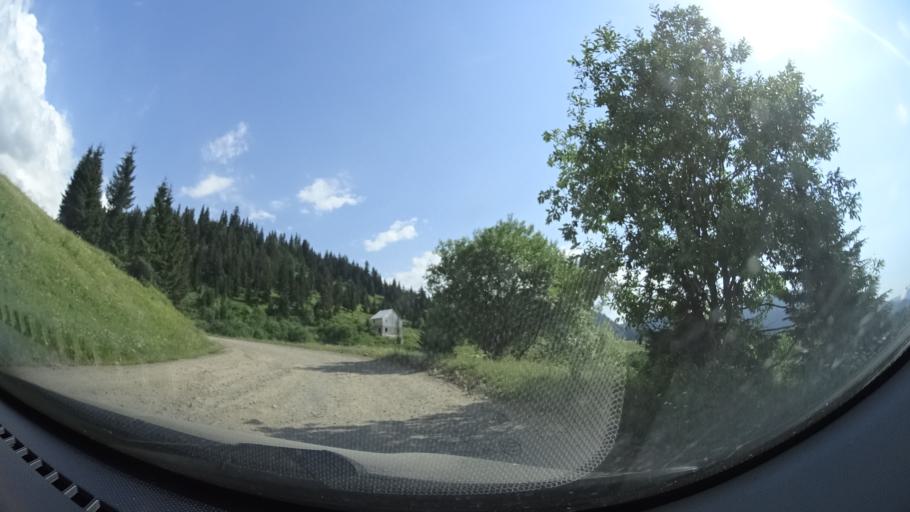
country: GE
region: Ajaria
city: Dioknisi
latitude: 41.6382
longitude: 42.4959
